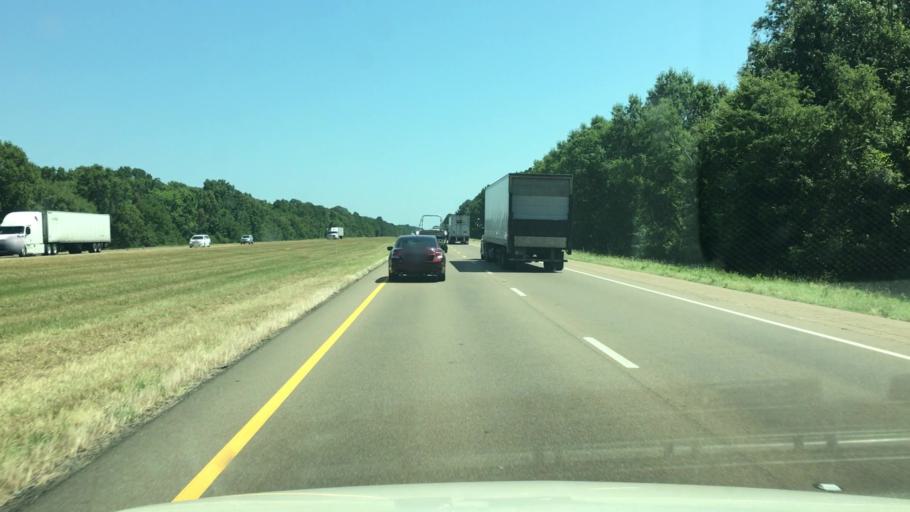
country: US
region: Texas
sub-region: Morris County
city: Naples
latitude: 33.3475
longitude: -94.6542
